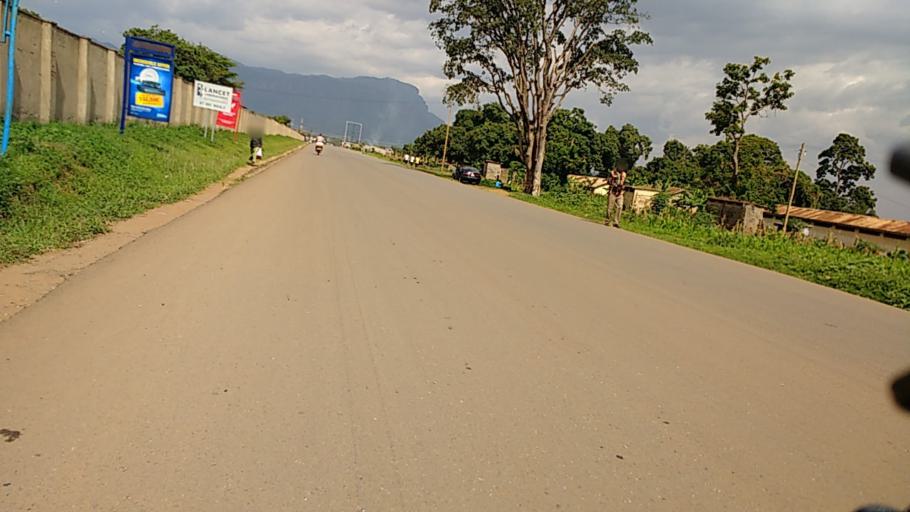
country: UG
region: Eastern Region
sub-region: Mbale District
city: Mbale
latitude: 1.0787
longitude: 34.1562
